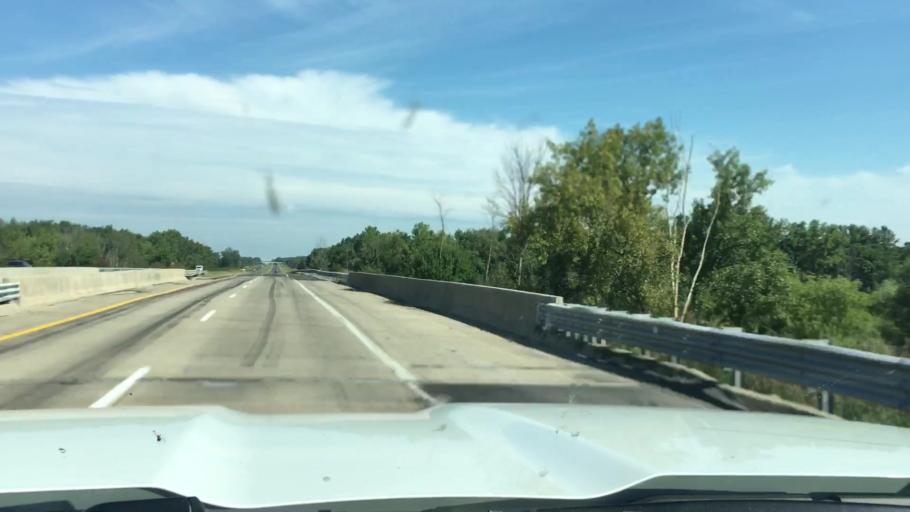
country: US
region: Michigan
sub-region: Saginaw County
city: Freeland
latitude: 43.5432
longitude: -84.1387
